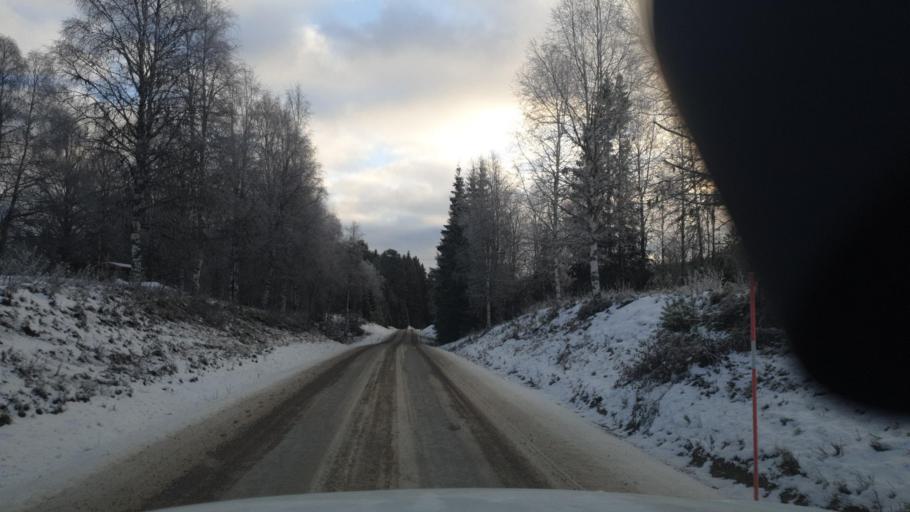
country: SE
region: Vaermland
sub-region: Eda Kommun
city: Charlottenberg
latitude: 60.0586
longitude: 12.5542
